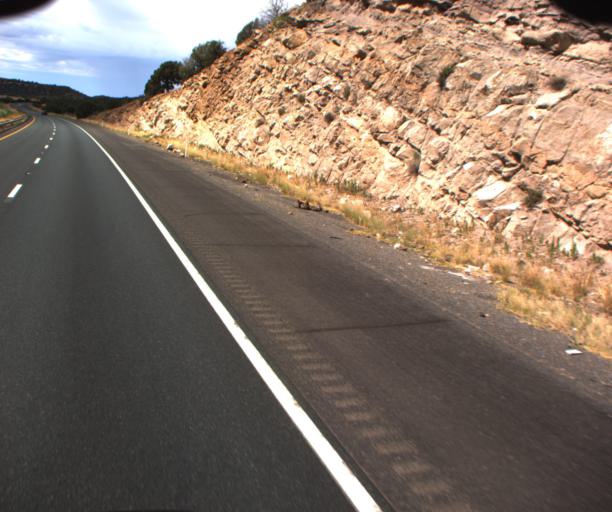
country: US
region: Arizona
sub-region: Yavapai County
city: Camp Verde
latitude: 34.4994
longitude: -112.0040
